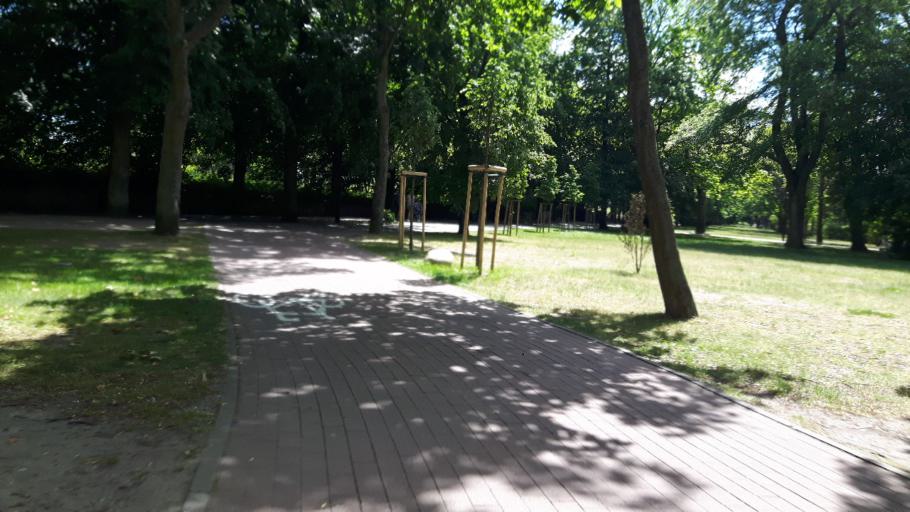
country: PL
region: Pomeranian Voivodeship
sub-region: Sopot
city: Sopot
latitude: 54.4527
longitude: 18.5640
